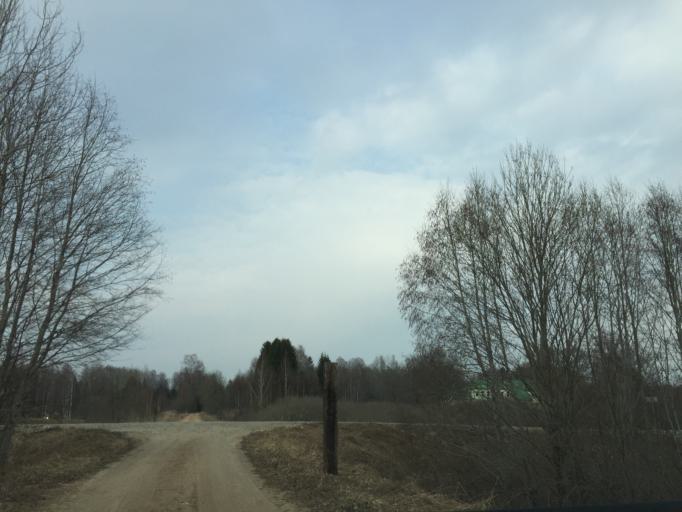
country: LV
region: Priekuli
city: Priekuli
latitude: 57.2124
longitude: 25.4110
